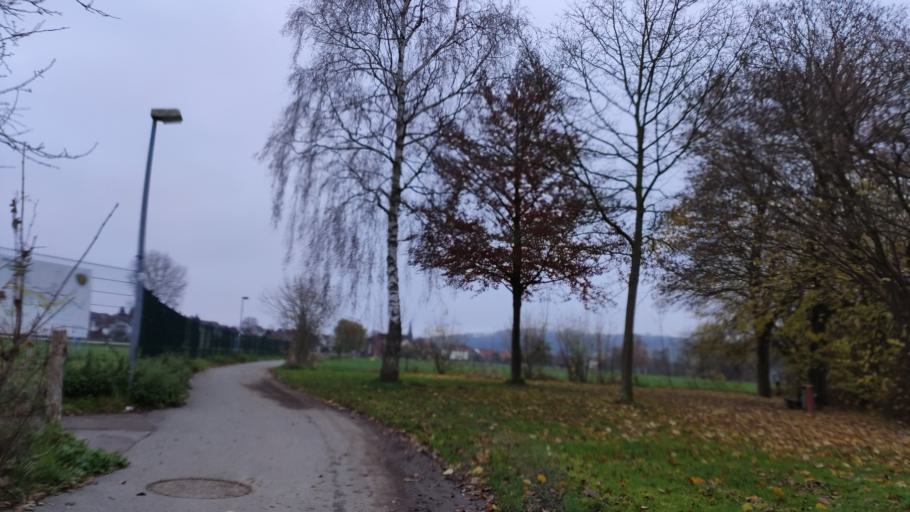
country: DE
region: North Rhine-Westphalia
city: Beverungen
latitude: 51.7077
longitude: 9.2958
